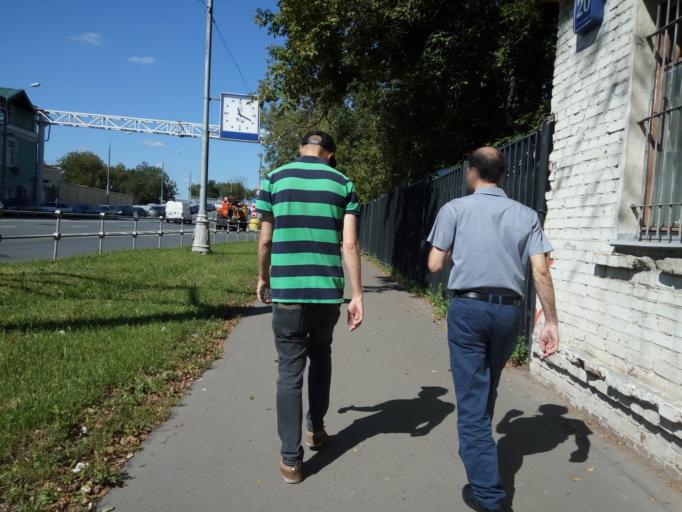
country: RU
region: Moscow
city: Sokol
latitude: 55.7715
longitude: 37.5169
